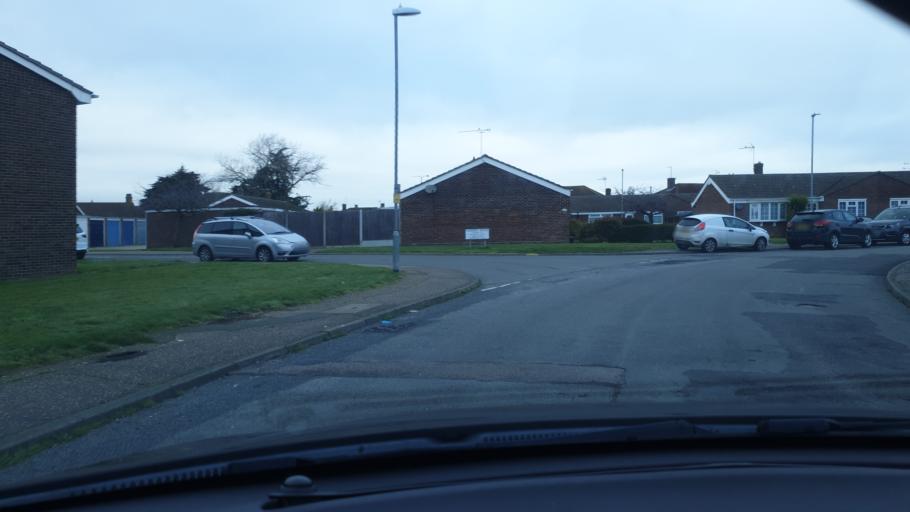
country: GB
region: England
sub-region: Essex
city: Walton-on-the-Naze
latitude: 51.8475
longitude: 1.2512
